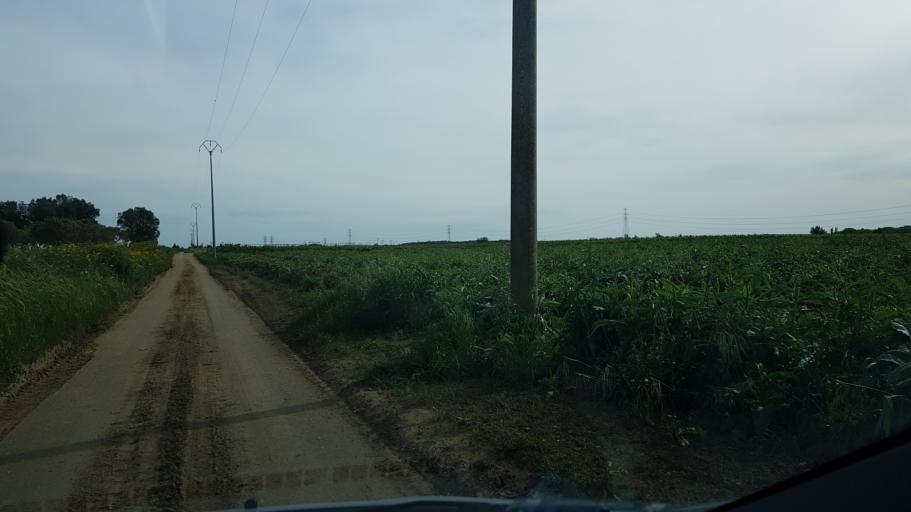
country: IT
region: Apulia
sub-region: Provincia di Brindisi
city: Tuturano
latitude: 40.5749
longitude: 17.9207
